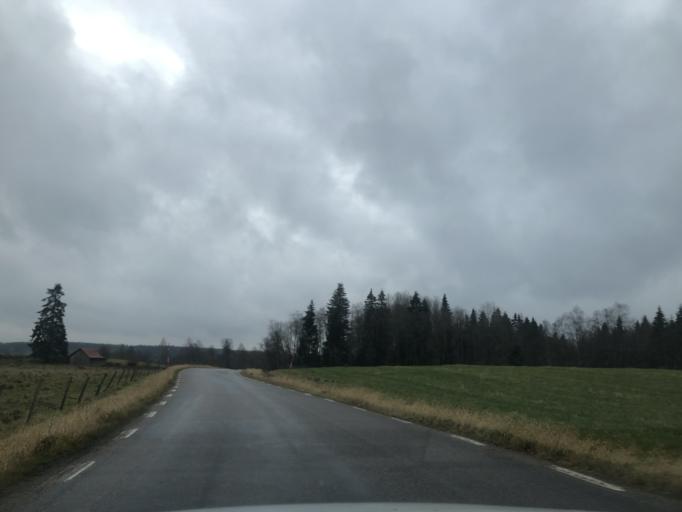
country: SE
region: Vaestra Goetaland
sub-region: Ulricehamns Kommun
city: Ulricehamn
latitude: 57.8918
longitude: 13.5100
